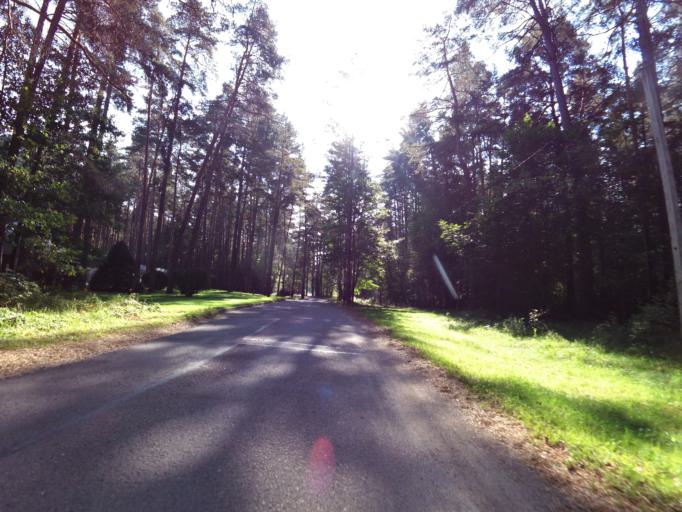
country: LT
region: Vilnius County
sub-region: Vilnius
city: Vilnius
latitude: 54.7345
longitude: 25.3091
